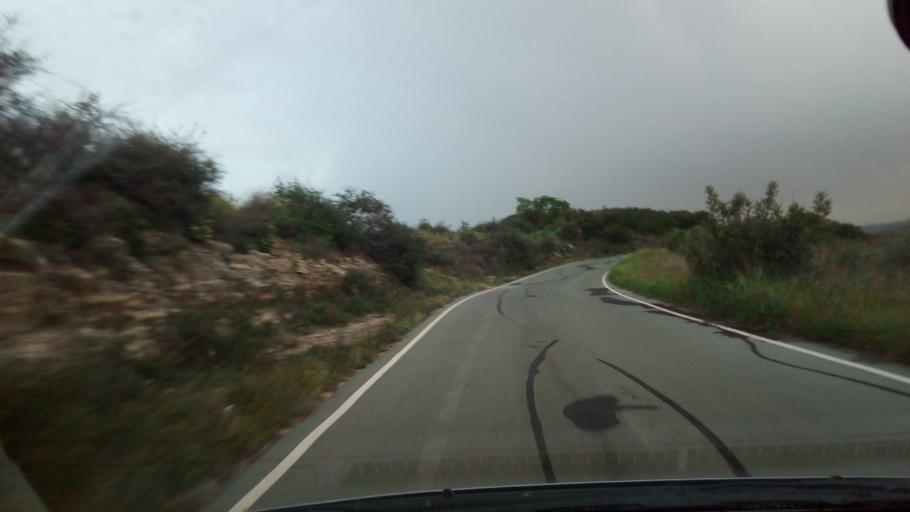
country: CY
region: Pafos
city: Polis
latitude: 34.9624
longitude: 32.4427
